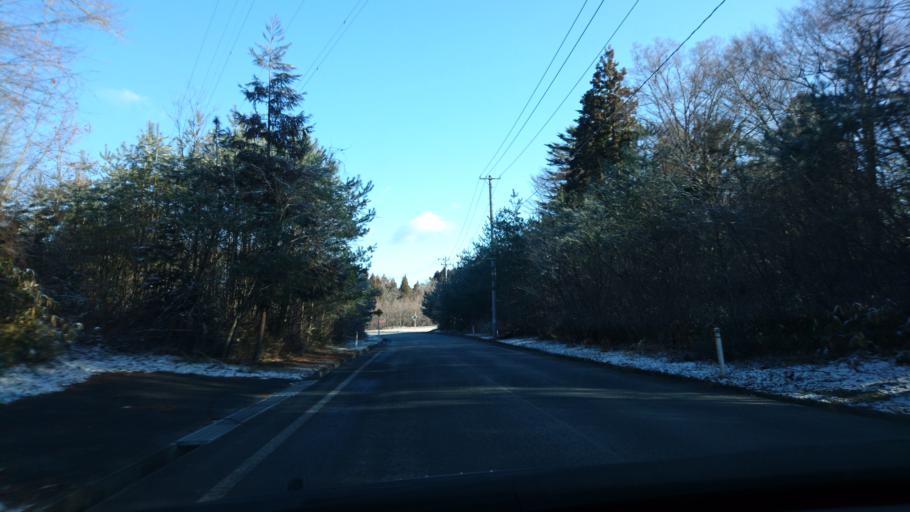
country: JP
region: Iwate
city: Ichinoseki
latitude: 38.8822
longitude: 141.3362
